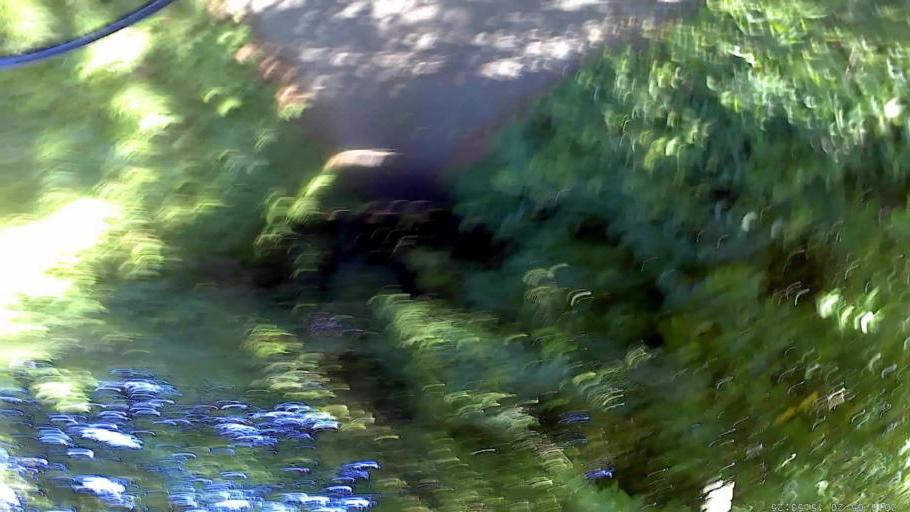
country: JP
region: Kanagawa
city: Hadano
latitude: 35.3276
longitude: 139.2029
